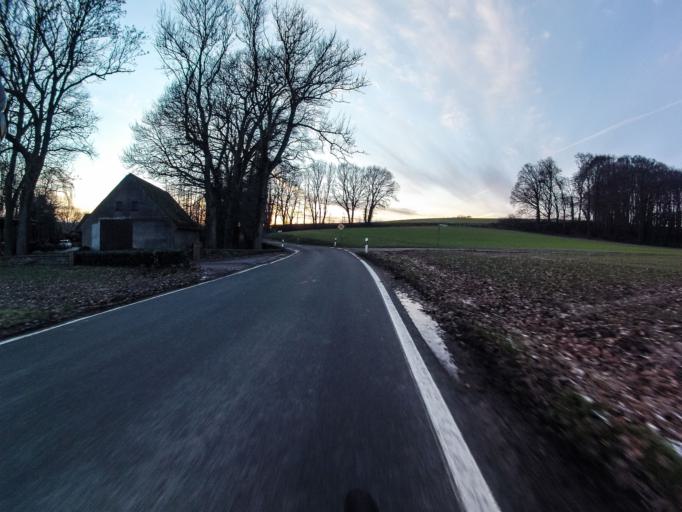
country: DE
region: North Rhine-Westphalia
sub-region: Regierungsbezirk Munster
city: Tecklenburg
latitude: 52.2663
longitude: 7.8456
